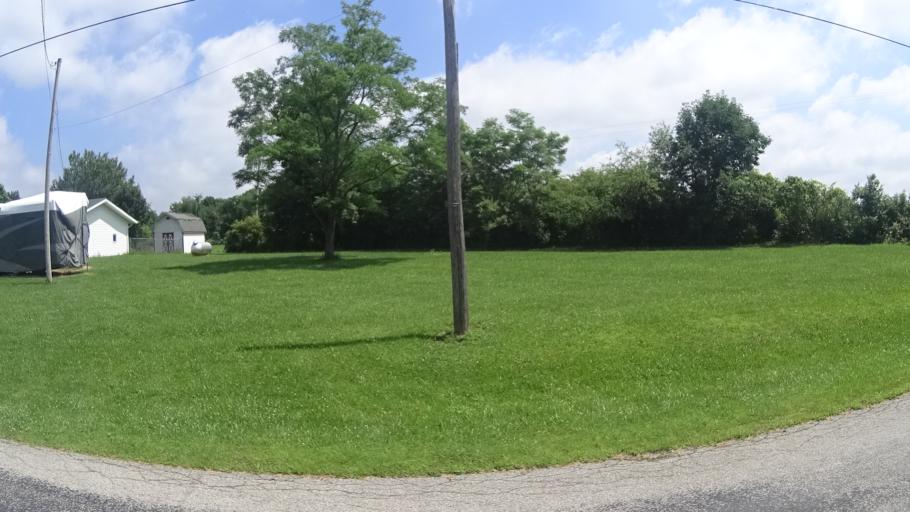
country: US
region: Ohio
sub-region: Huron County
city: Wakeman
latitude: 41.3042
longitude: -82.3586
